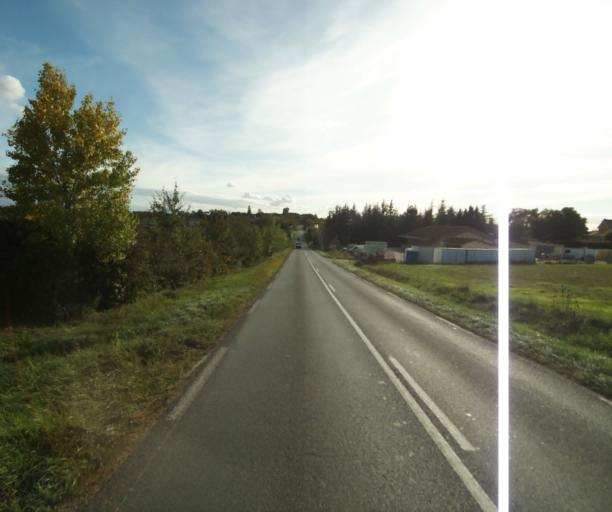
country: FR
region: Midi-Pyrenees
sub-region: Departement du Gers
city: Gondrin
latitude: 43.8928
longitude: 0.2433
